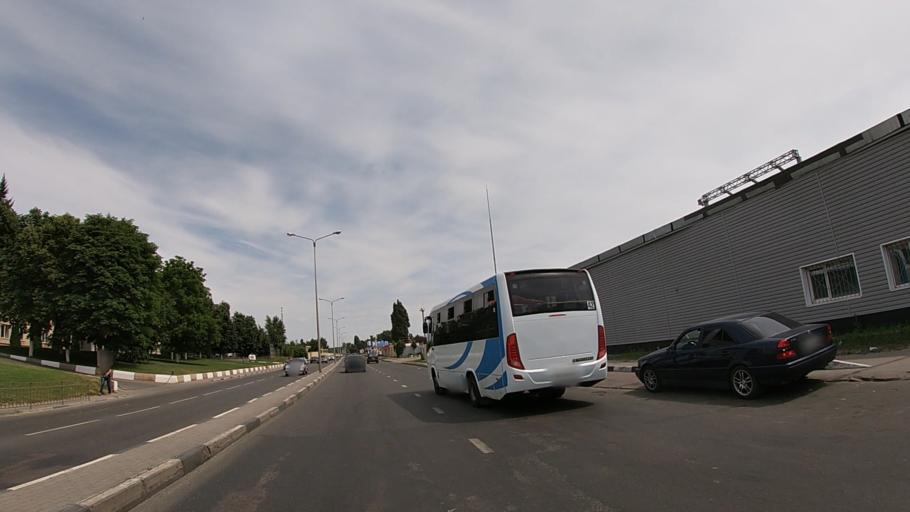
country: RU
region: Belgorod
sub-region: Belgorodskiy Rayon
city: Belgorod
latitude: 50.6137
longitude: 36.5361
